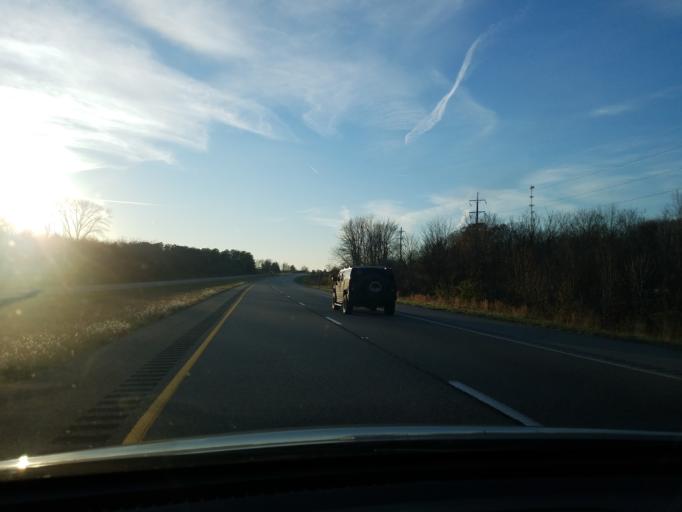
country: US
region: Indiana
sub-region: Warrick County
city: Boonville
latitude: 38.1999
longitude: -87.2545
